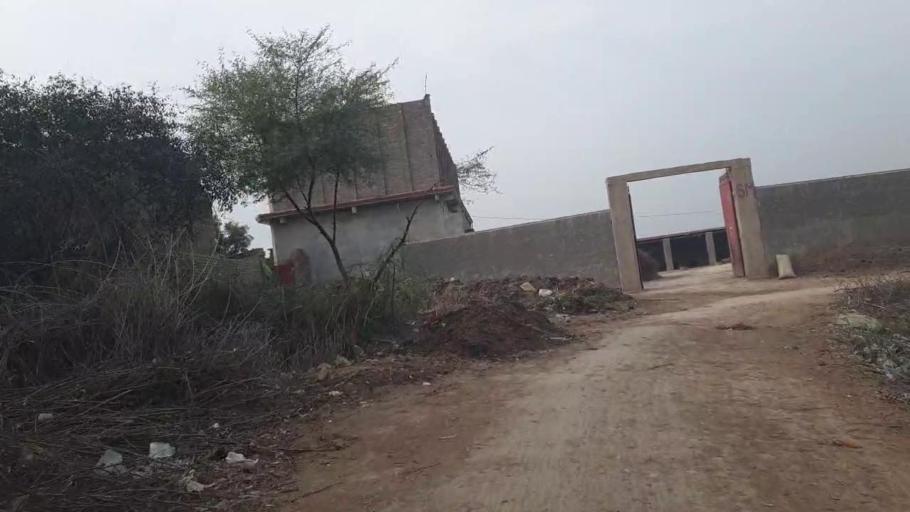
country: PK
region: Sindh
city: Shahdadpur
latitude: 25.9503
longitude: 68.7061
